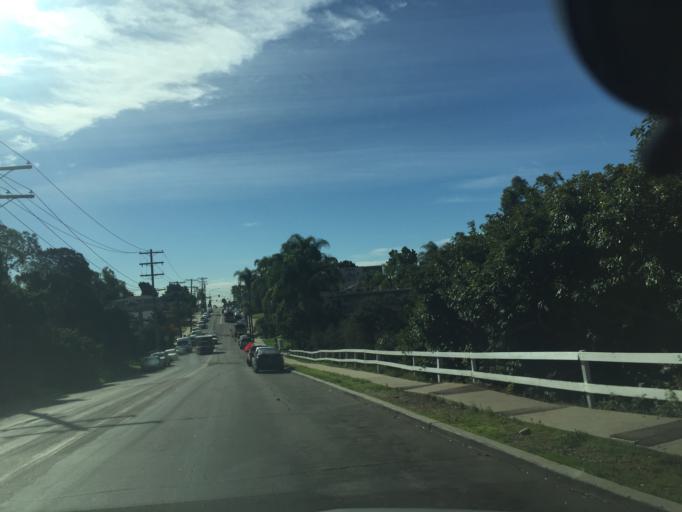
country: US
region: California
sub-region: San Diego County
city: Lemon Grove
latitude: 32.7619
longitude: -117.0794
